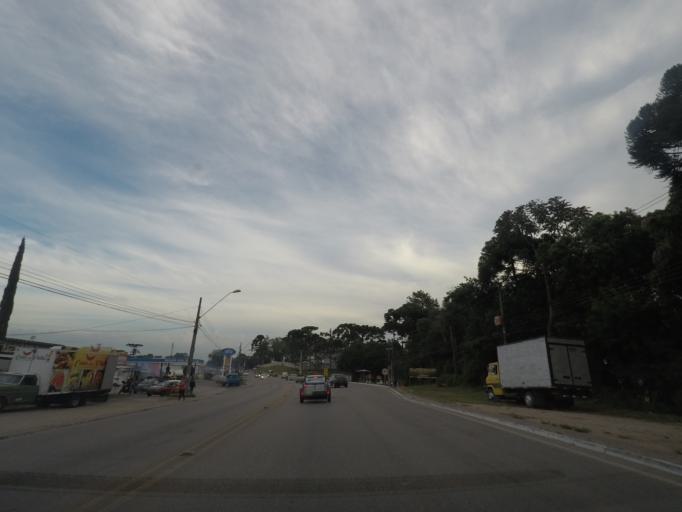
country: BR
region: Parana
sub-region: Colombo
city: Colombo
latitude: -25.3474
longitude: -49.2208
